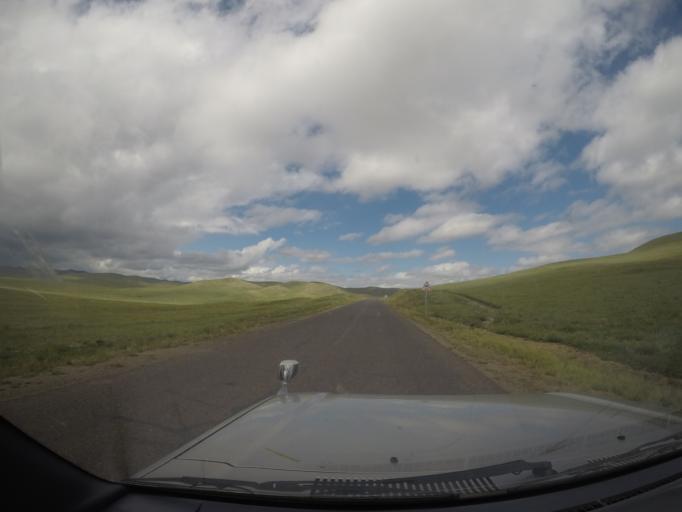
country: MN
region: Hentiy
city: Modot
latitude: 47.8087
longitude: 108.7886
